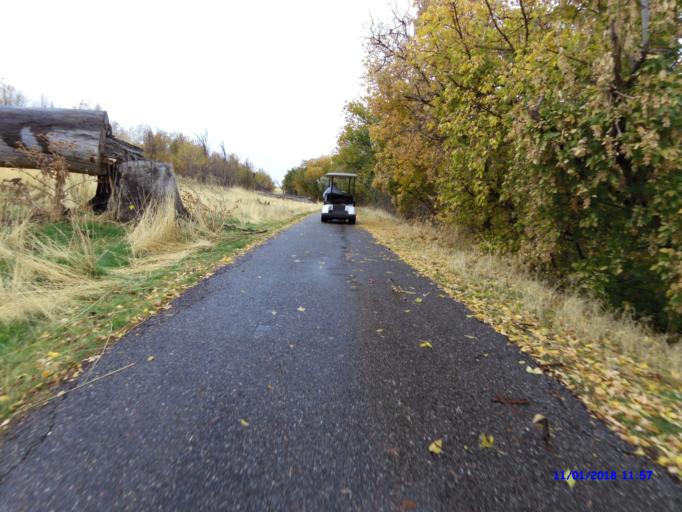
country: US
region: Utah
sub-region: Weber County
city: Ogden
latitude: 41.2343
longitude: -111.9969
